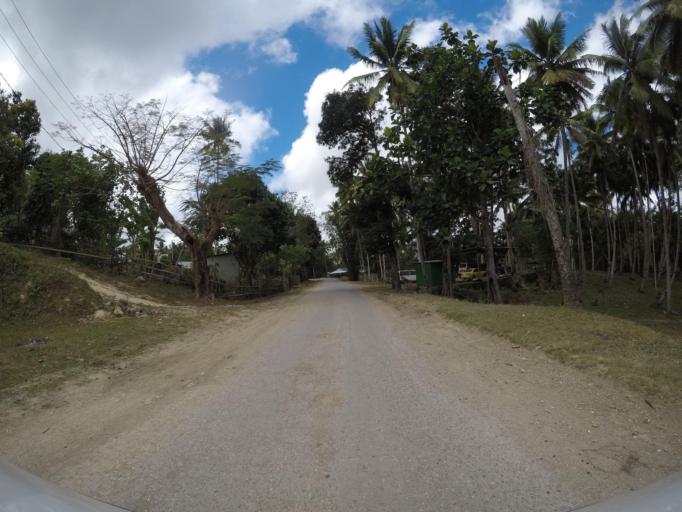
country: TL
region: Lautem
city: Lospalos
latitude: -8.4397
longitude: 126.9751
